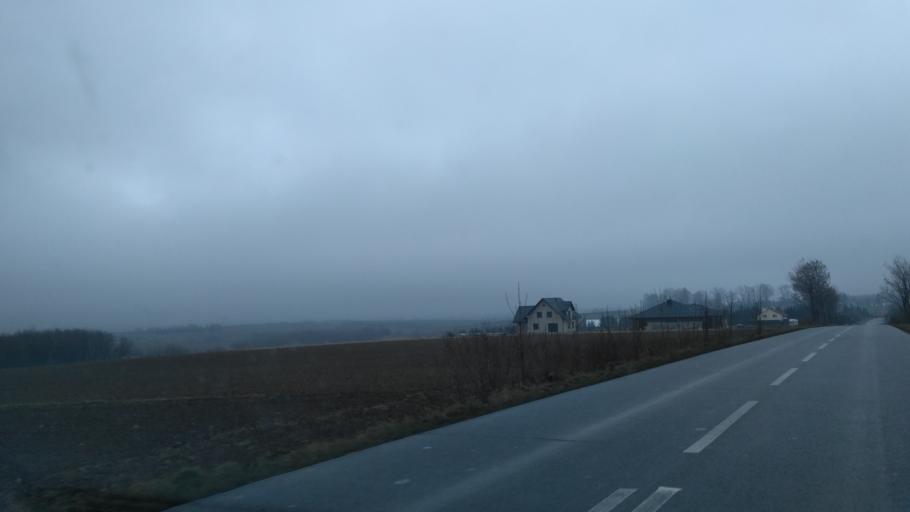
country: PL
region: Subcarpathian Voivodeship
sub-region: Powiat jaroslawski
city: Pruchnik
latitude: 49.9064
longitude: 22.4989
